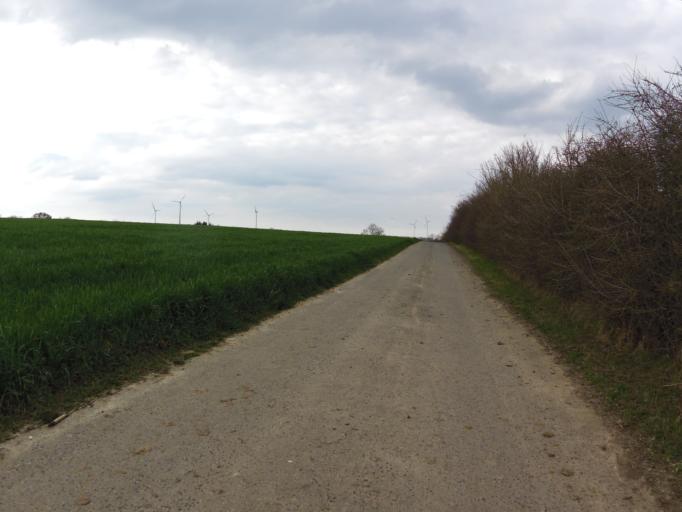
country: DE
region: Bavaria
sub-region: Regierungsbezirk Unterfranken
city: Buchbrunn
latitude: 49.7421
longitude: 10.1204
